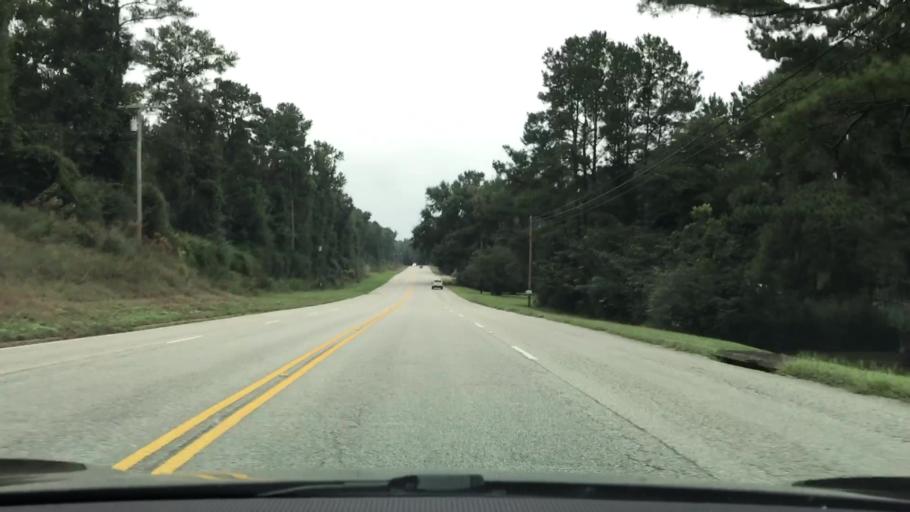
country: US
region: Alabama
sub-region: Coffee County
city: Elba
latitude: 31.4475
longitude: -86.0713
